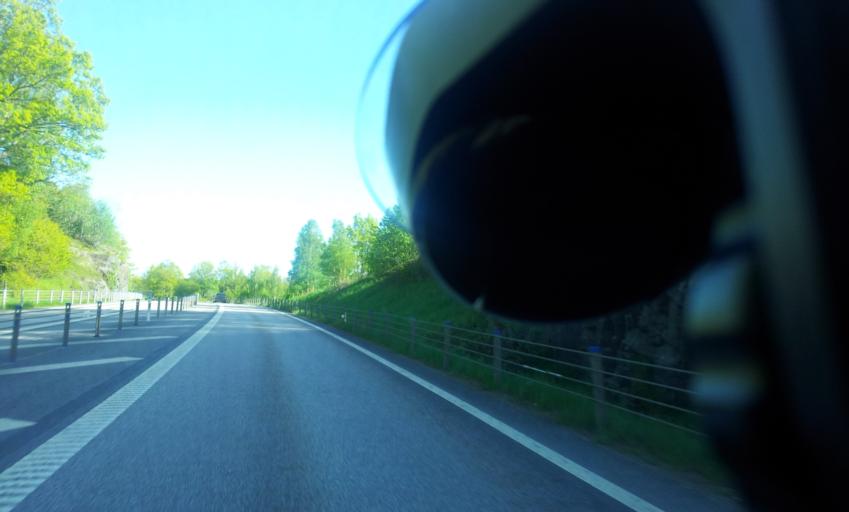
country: SE
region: Kalmar
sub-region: Vasterviks Kommun
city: Gamleby
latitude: 57.8847
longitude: 16.3881
